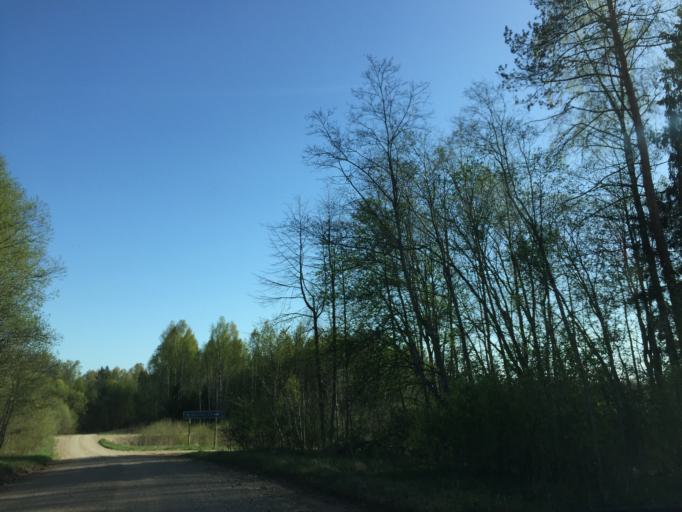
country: LV
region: Ergli
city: Ergli
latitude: 56.8909
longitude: 25.4910
